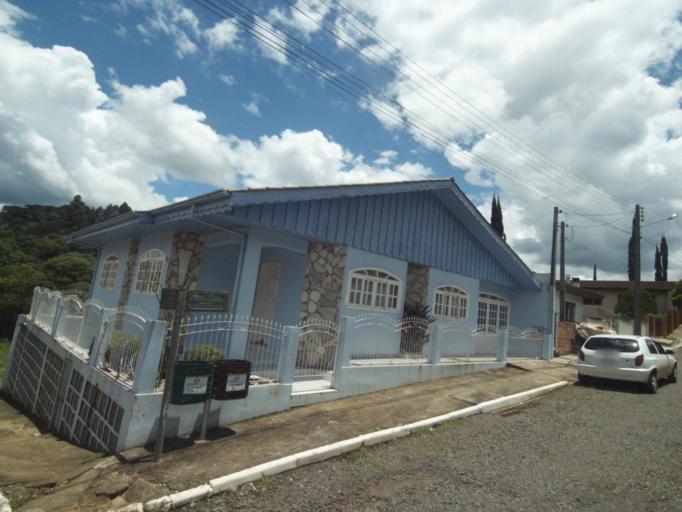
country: BR
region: Parana
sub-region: Pinhao
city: Pinhao
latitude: -26.1557
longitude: -51.5566
